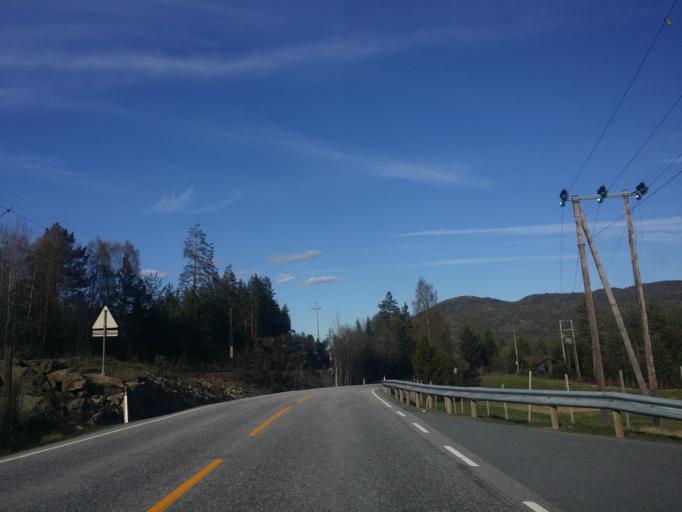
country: NO
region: Telemark
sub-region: Notodden
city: Notodden
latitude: 59.6108
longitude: 9.4524
